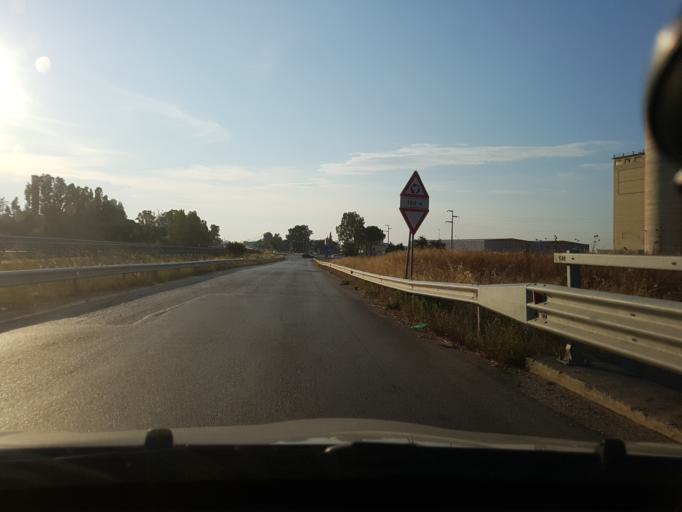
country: IT
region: Apulia
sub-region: Provincia di Foggia
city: Carapelle
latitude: 41.4012
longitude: 15.6517
